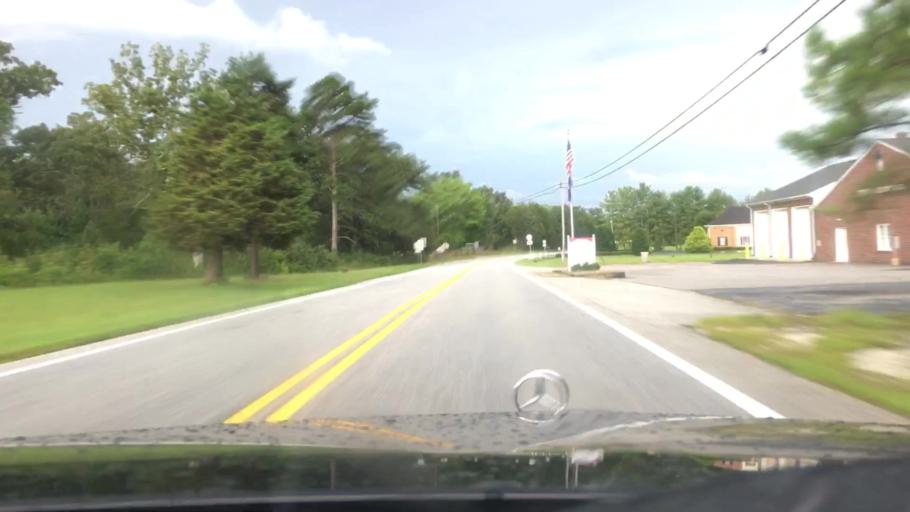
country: US
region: Virginia
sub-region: Nelson County
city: Lovingston
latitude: 37.7636
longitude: -78.9786
